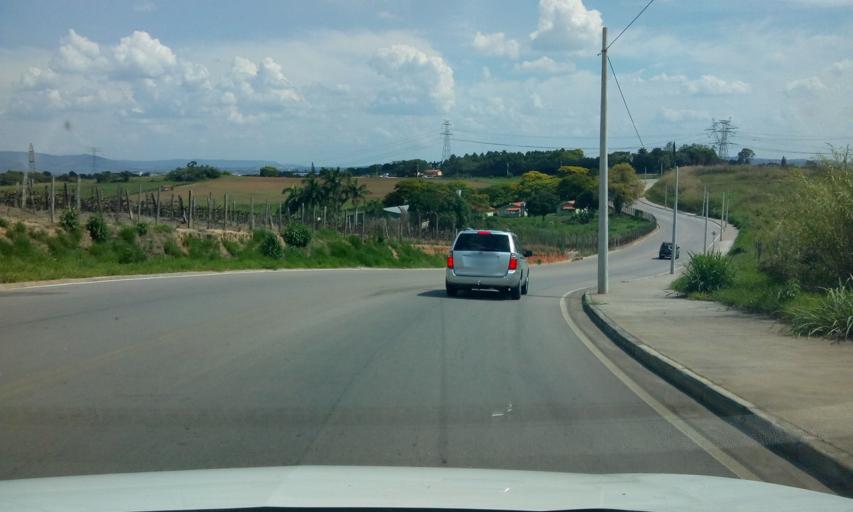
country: BR
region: Sao Paulo
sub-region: Louveira
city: Louveira
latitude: -23.1176
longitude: -47.0036
